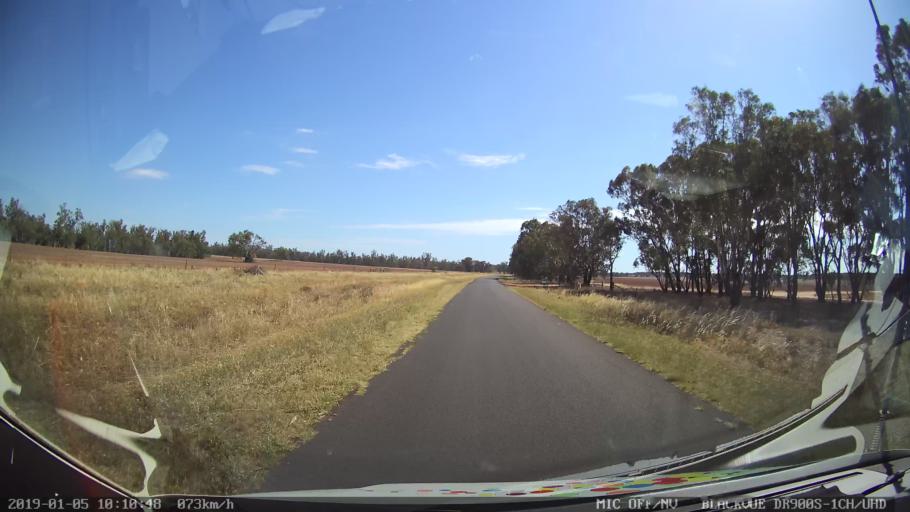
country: AU
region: New South Wales
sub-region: Gilgandra
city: Gilgandra
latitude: -31.6184
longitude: 148.8956
